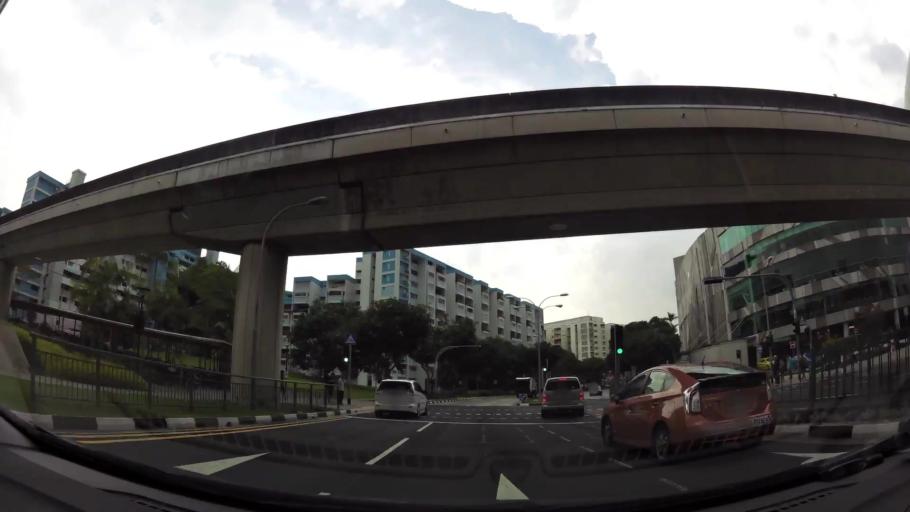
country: SG
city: Singapore
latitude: 1.3526
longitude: 103.9458
